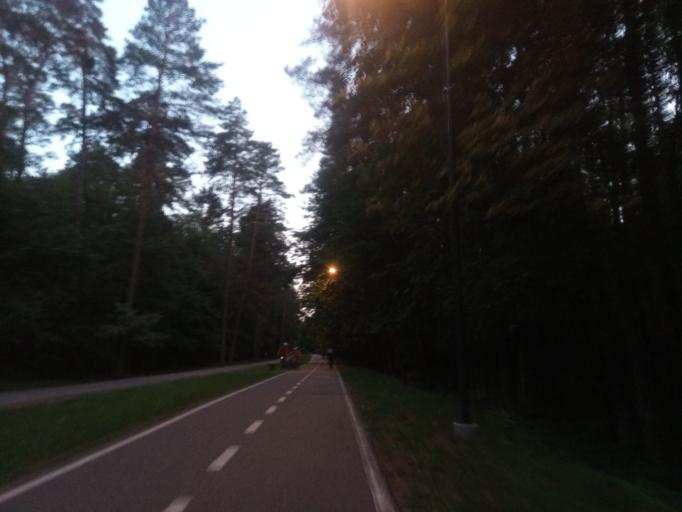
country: LT
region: Vilnius County
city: Vilkpede
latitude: 54.6883
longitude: 25.2365
